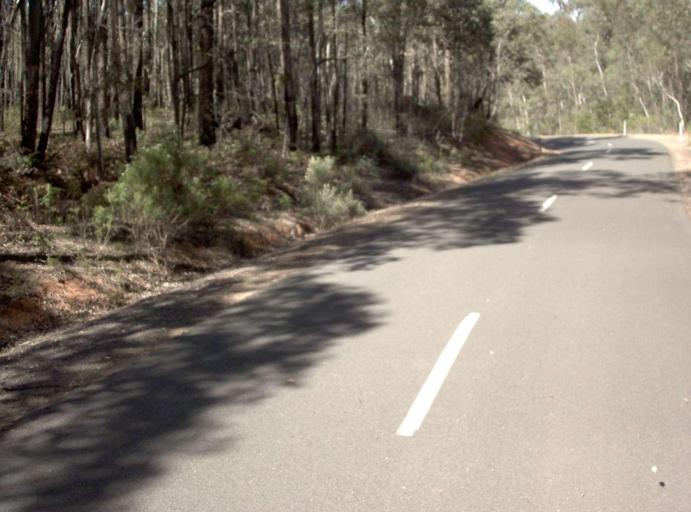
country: AU
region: New South Wales
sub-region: Bombala
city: Bombala
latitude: -37.0926
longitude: 148.7659
